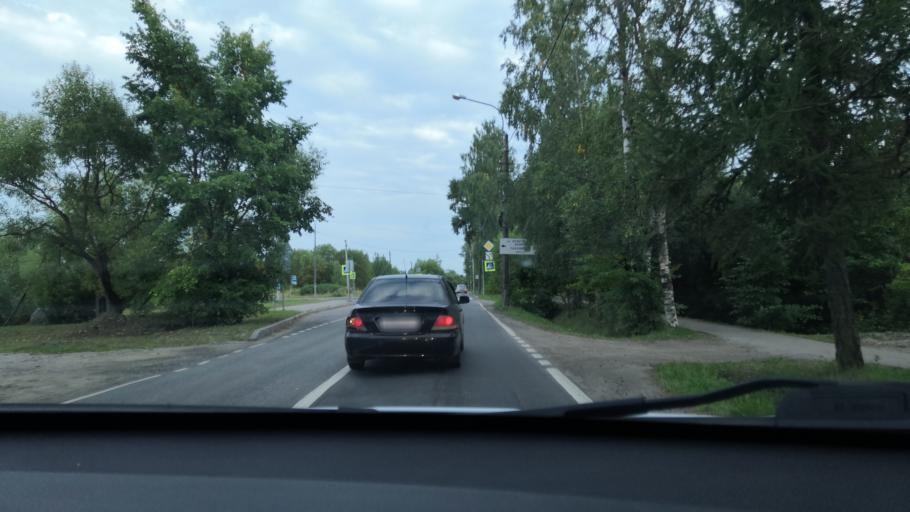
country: RU
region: St.-Petersburg
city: Pushkin
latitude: 59.6962
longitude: 30.4122
